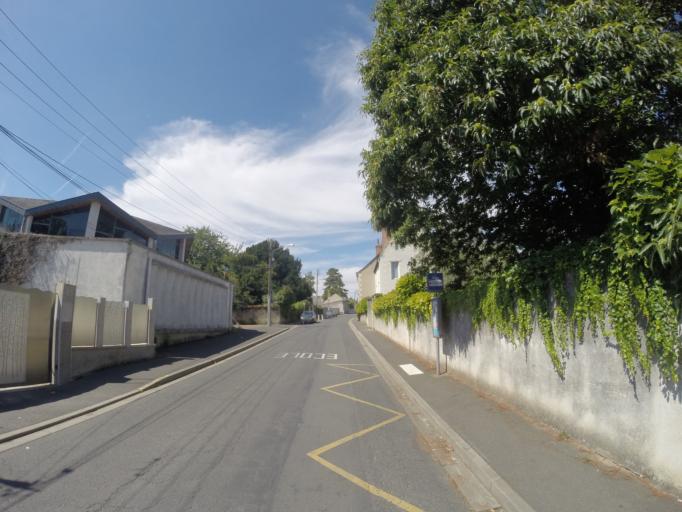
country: FR
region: Centre
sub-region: Departement d'Indre-et-Loire
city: Tours
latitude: 47.4095
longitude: 0.7132
